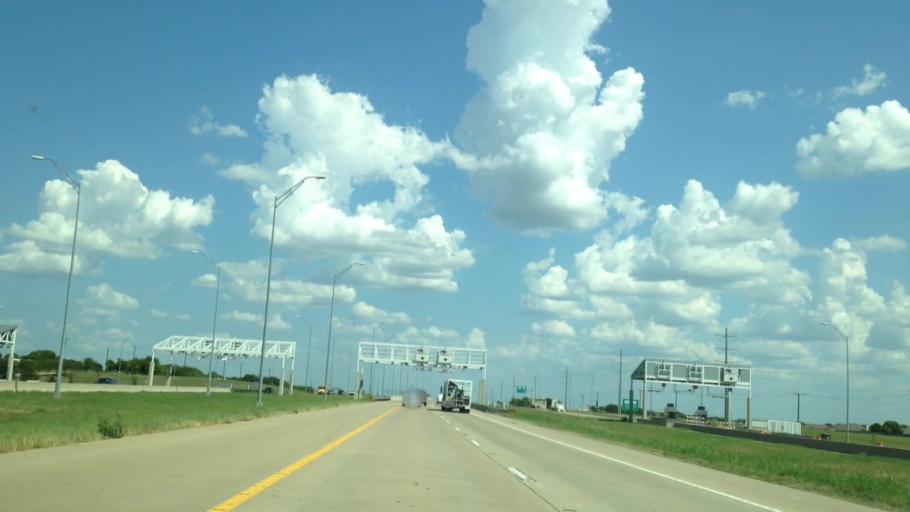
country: US
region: Texas
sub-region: Travis County
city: Windemere
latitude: 30.4831
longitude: -97.6125
